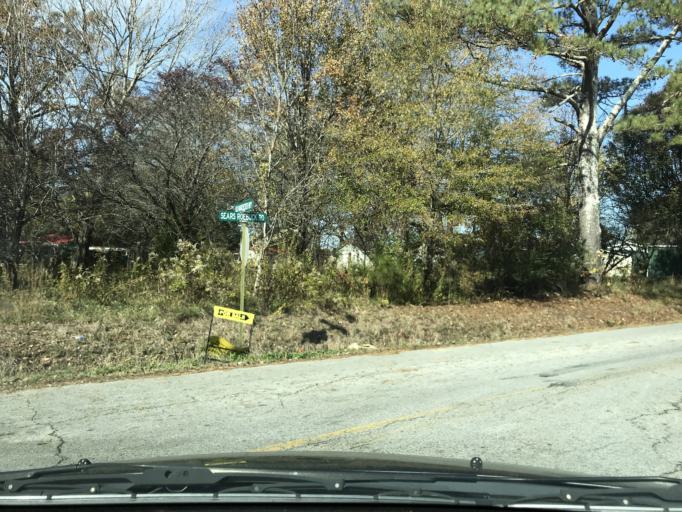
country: US
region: Tennessee
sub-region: Coffee County
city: Tullahoma
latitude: 35.3894
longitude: -86.1643
